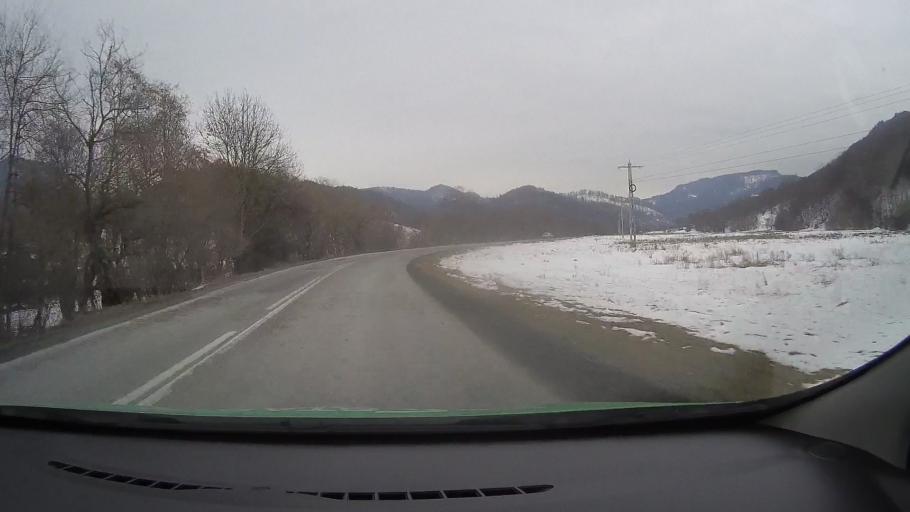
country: RO
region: Brasov
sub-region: Oras Rasnov
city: Rasnov
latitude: 45.5479
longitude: 25.4956
